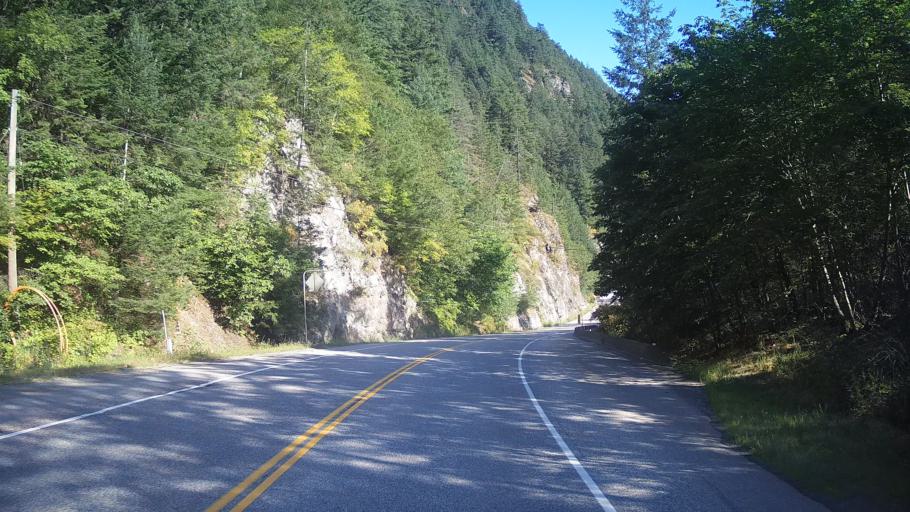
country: CA
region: British Columbia
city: Hope
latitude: 49.5692
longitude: -121.4029
